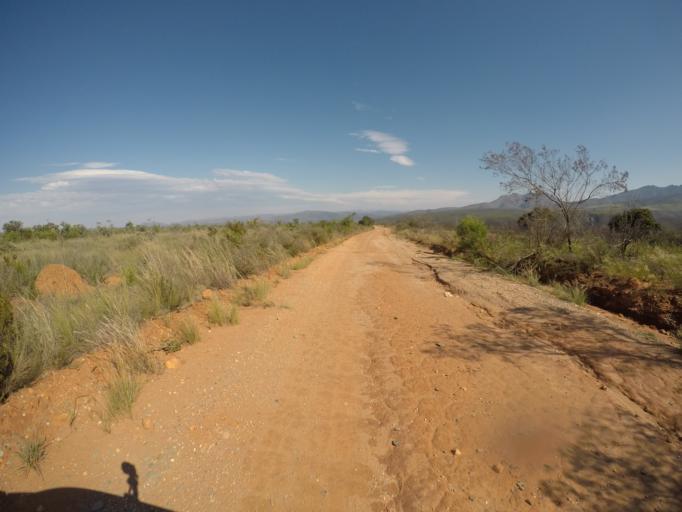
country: ZA
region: Eastern Cape
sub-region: Cacadu District Municipality
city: Kareedouw
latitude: -33.6362
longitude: 24.4598
